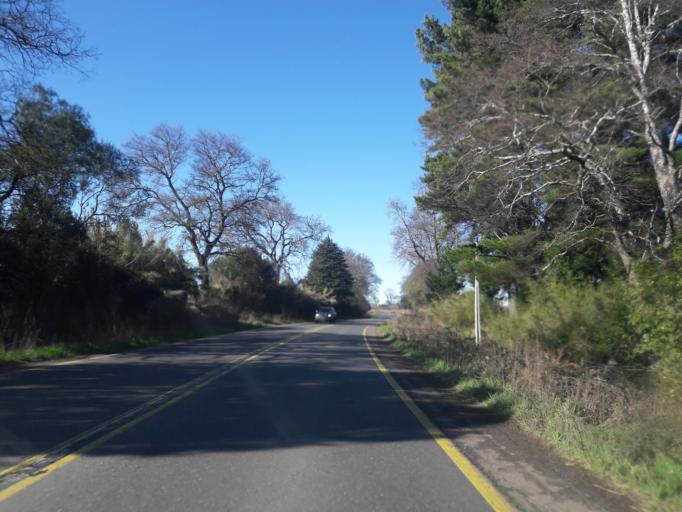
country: CL
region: Araucania
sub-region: Provincia de Malleco
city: Victoria
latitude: -38.2521
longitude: -72.2949
